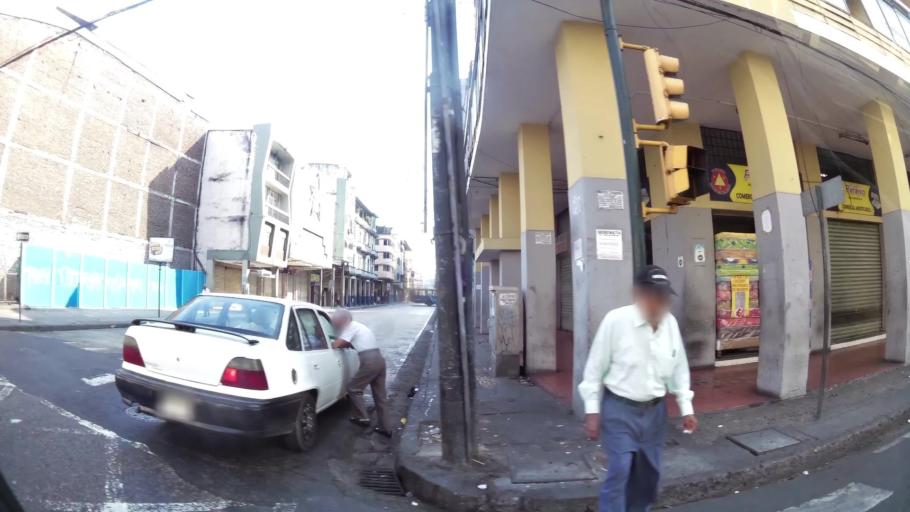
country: EC
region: Guayas
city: Guayaquil
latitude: -2.1959
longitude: -79.8868
